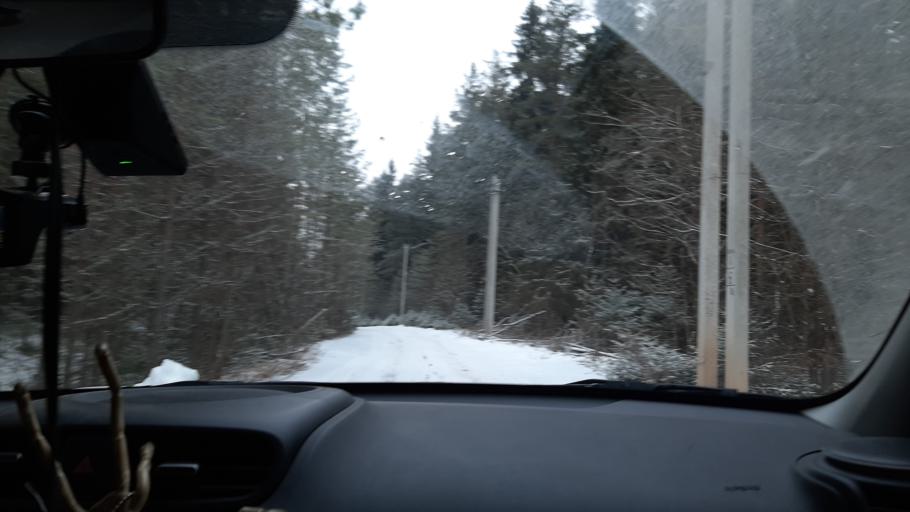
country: RU
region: Ivanovo
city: Kokhma
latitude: 56.8979
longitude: 41.0112
